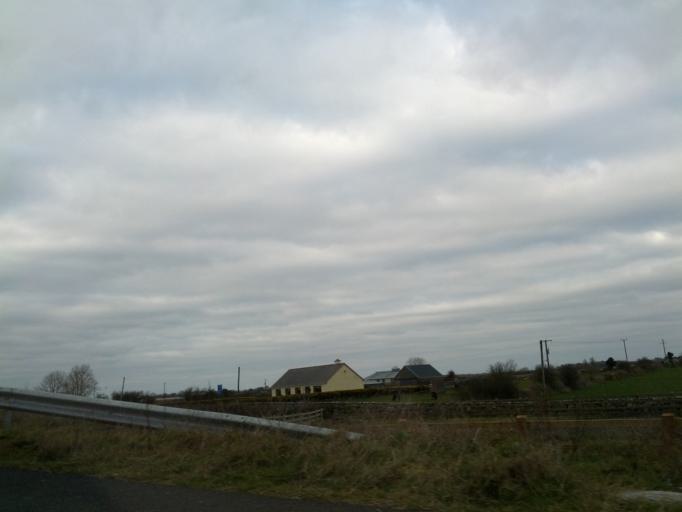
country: IE
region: Connaught
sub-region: County Galway
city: Gort
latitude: 53.1639
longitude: -8.8507
